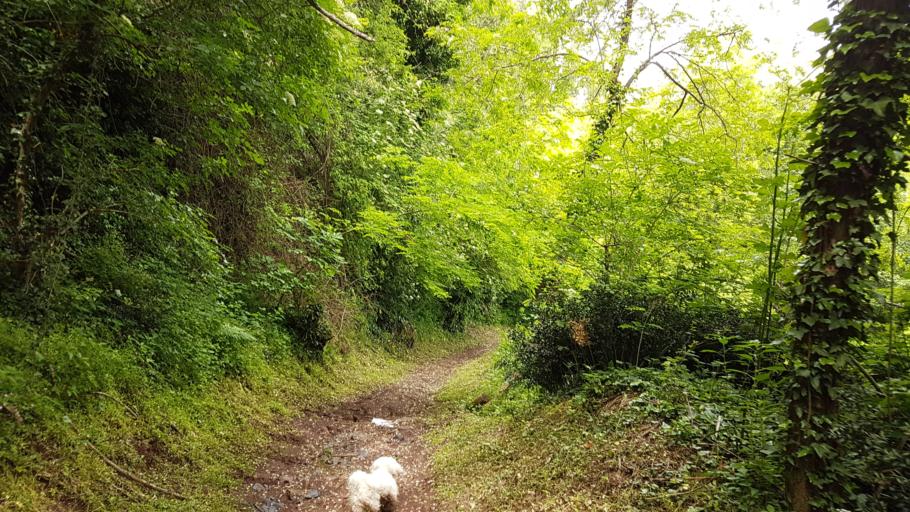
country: IT
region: Veneto
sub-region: Provincia di Vicenza
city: Arzignano
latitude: 45.5477
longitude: 11.3322
